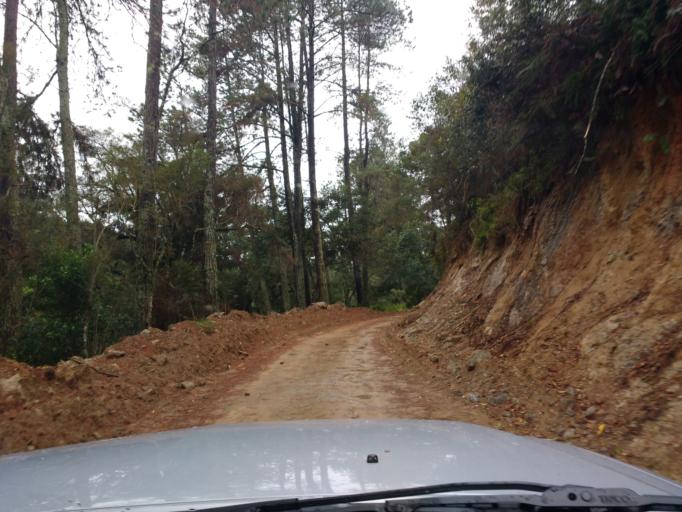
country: BR
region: Minas Gerais
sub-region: Cambui
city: Cambui
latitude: -22.7480
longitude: -45.9237
